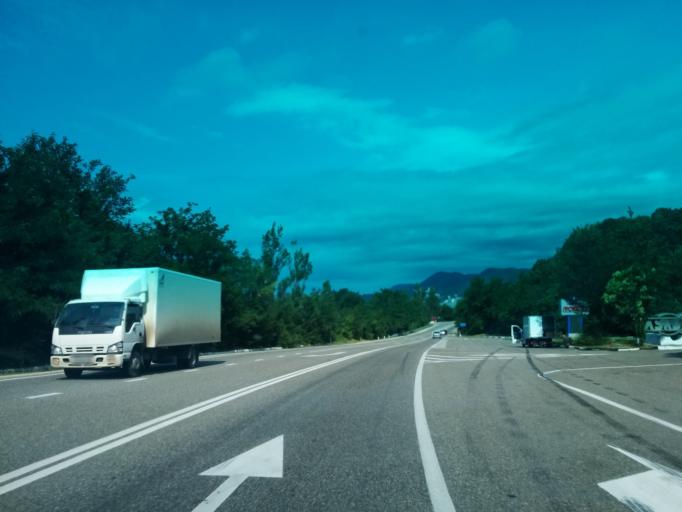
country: RU
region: Krasnodarskiy
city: Nebug
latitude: 44.1538
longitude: 39.0093
